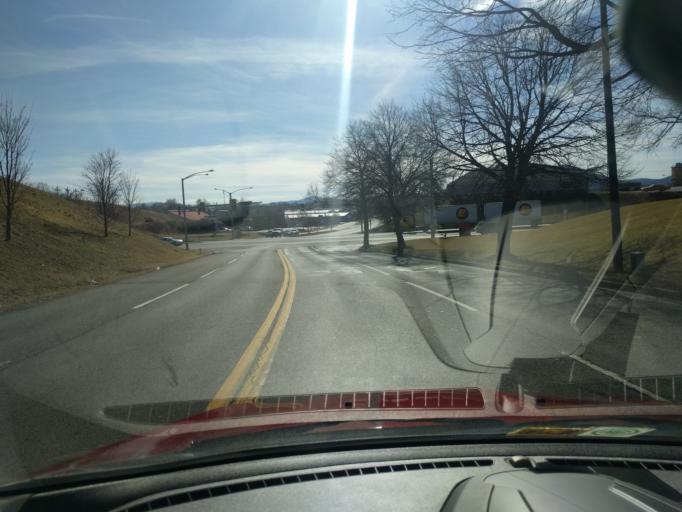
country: US
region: Virginia
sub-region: City of Roanoke
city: Roanoke
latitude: 37.2832
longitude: -79.9298
